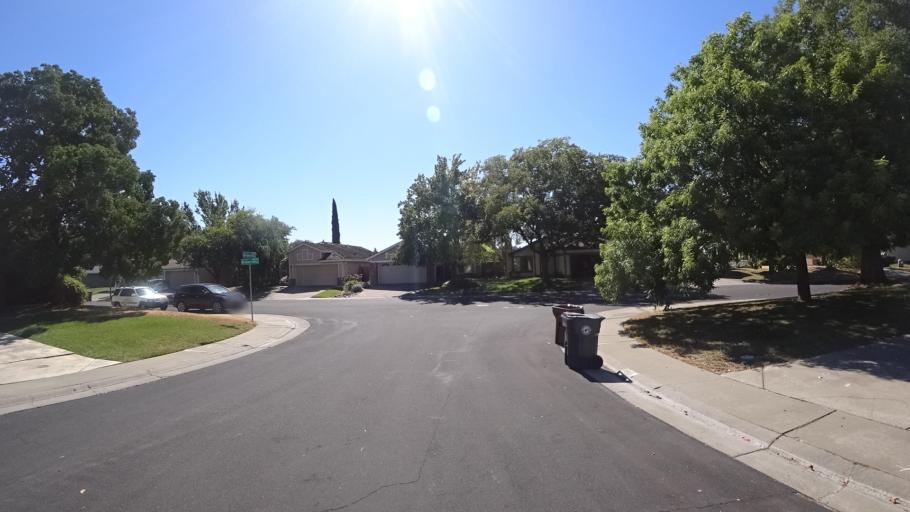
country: US
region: California
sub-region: Sacramento County
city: Laguna
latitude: 38.4266
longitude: -121.4285
